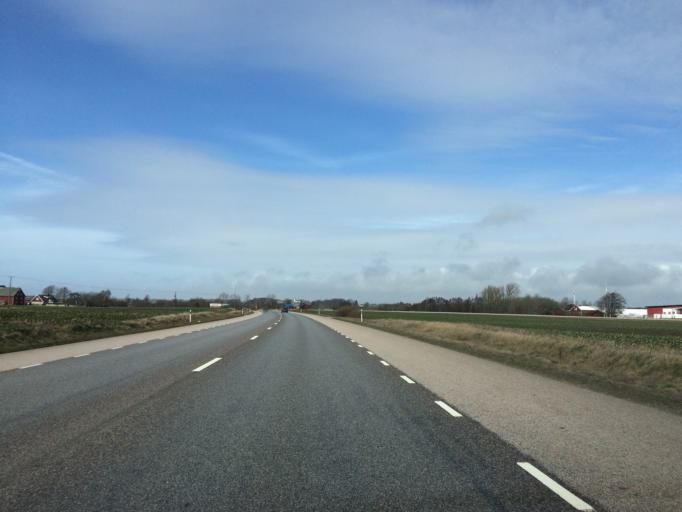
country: SE
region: Halland
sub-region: Laholms Kommun
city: Veinge
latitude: 56.5693
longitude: 13.0234
